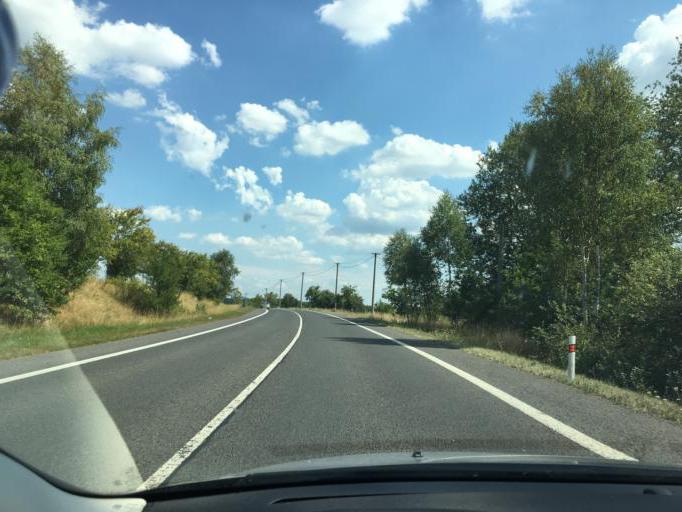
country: CZ
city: Jablonne v Podjestedi
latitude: 50.7714
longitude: 14.7271
